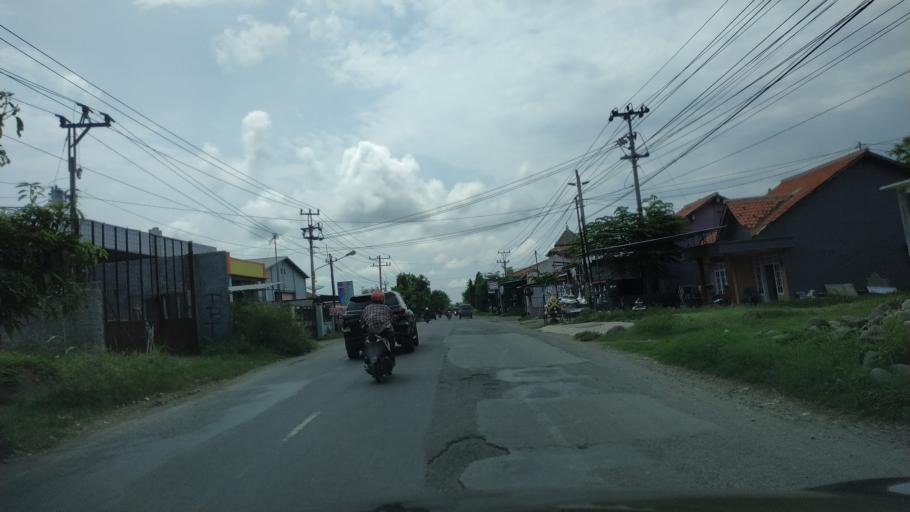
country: ID
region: Central Java
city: Adiwerna
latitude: -6.9204
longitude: 109.1262
